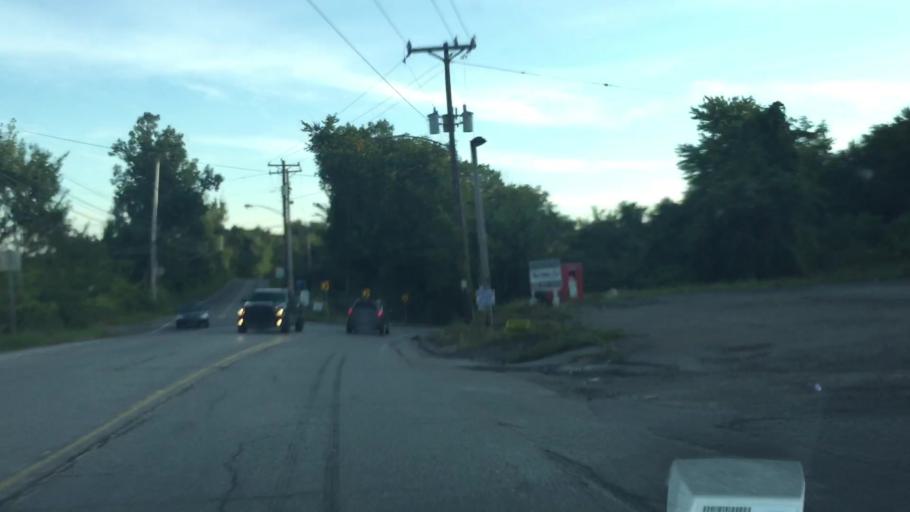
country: US
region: Pennsylvania
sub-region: Beaver County
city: Ambridge
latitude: 40.5613
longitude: -80.2752
